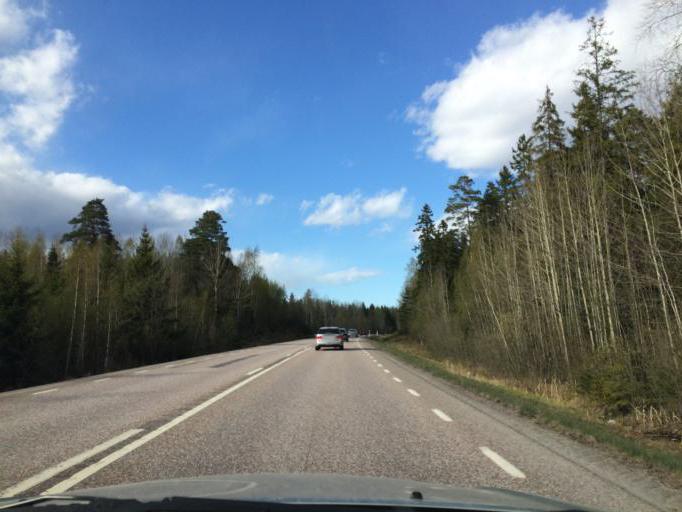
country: SE
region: Soedermanland
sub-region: Eskilstuna Kommun
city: Kvicksund
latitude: 59.5013
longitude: 16.3038
